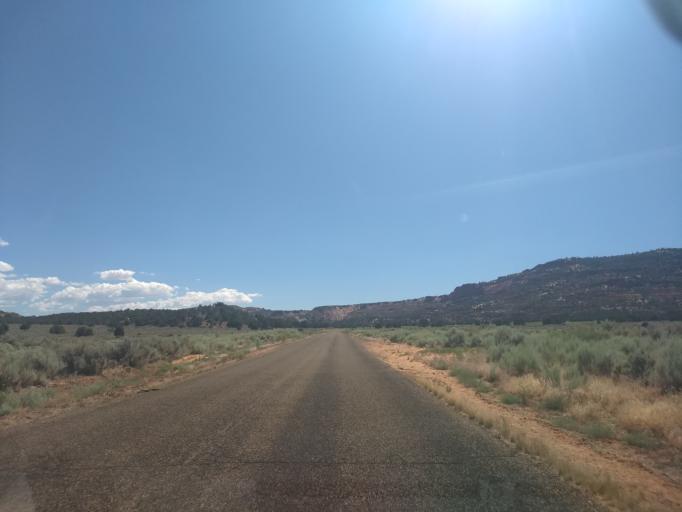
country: US
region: Utah
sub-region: Washington County
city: Hildale
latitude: 37.0114
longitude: -112.8469
